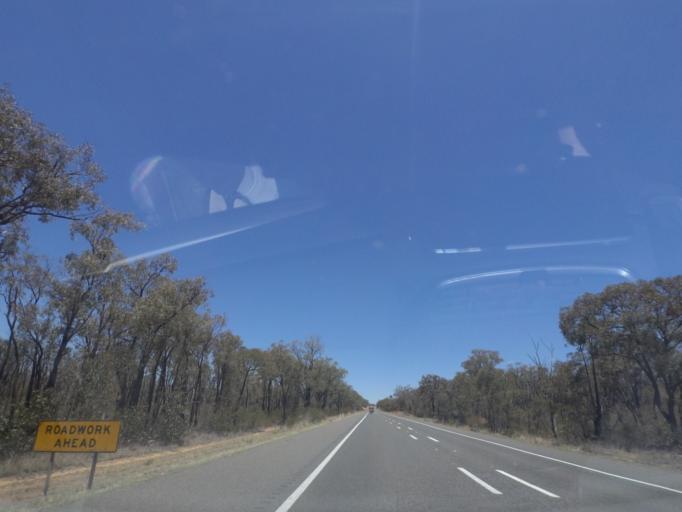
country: AU
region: New South Wales
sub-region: Warrumbungle Shire
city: Coonabarabran
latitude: -30.9123
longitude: 149.4355
